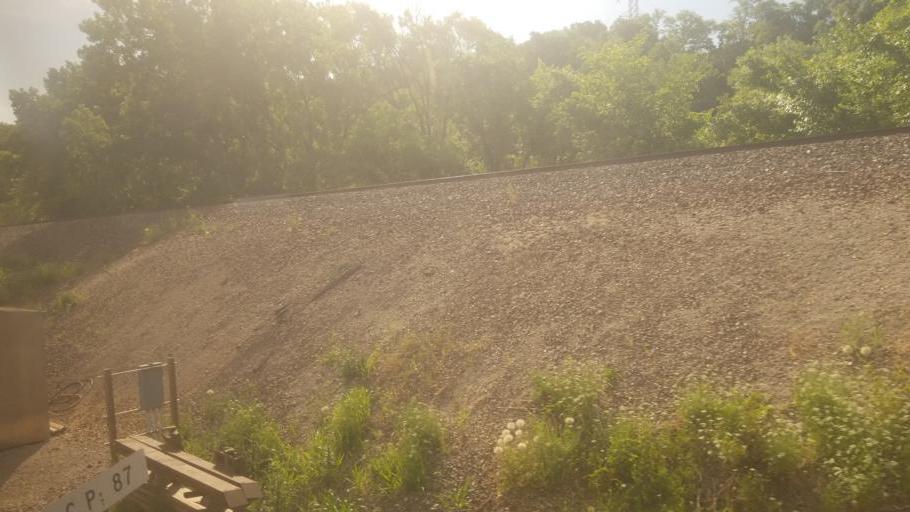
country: US
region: Kansas
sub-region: Johnson County
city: Shawnee
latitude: 39.0742
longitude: -94.7314
